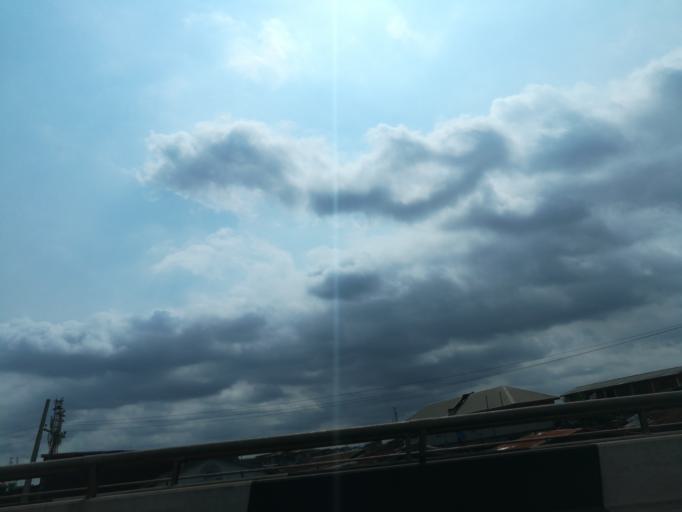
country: NG
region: Lagos
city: Somolu
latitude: 6.5377
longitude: 3.4003
